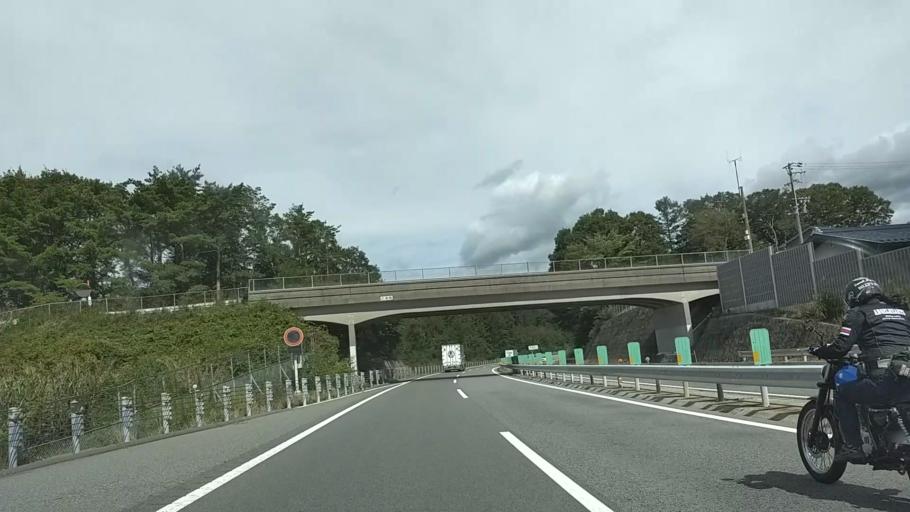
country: JP
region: Nagano
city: Chino
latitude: 35.9082
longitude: 138.2567
